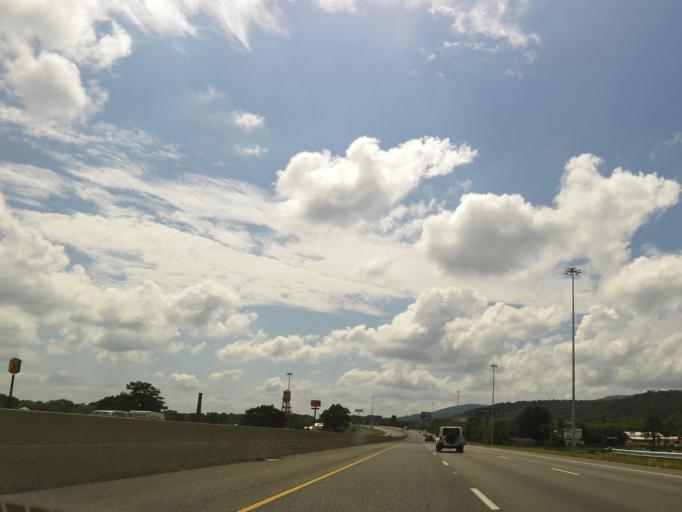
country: US
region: Alabama
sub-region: Calhoun County
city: Oxford
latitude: 33.6051
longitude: -85.8320
